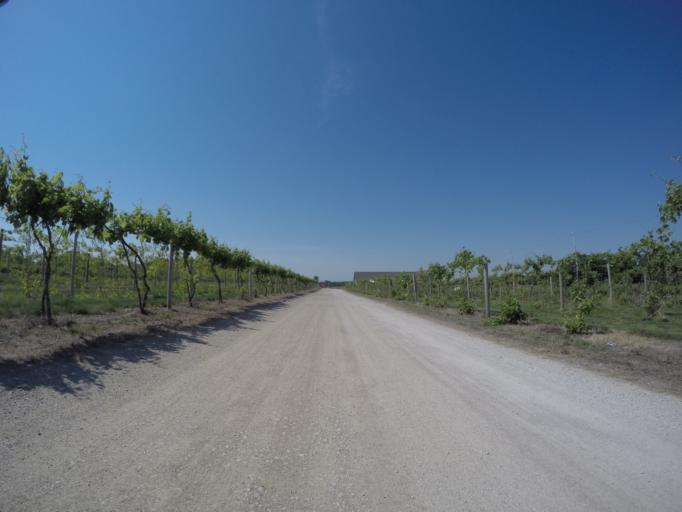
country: US
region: Nebraska
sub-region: Pawnee County
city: Pawnee City
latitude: 40.1159
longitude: -96.1629
